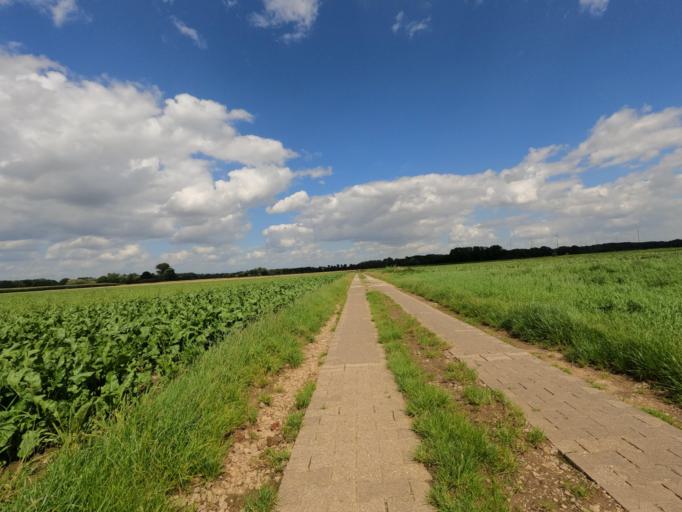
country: DE
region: North Rhine-Westphalia
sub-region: Regierungsbezirk Koln
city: Linnich
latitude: 51.0105
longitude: 6.2457
